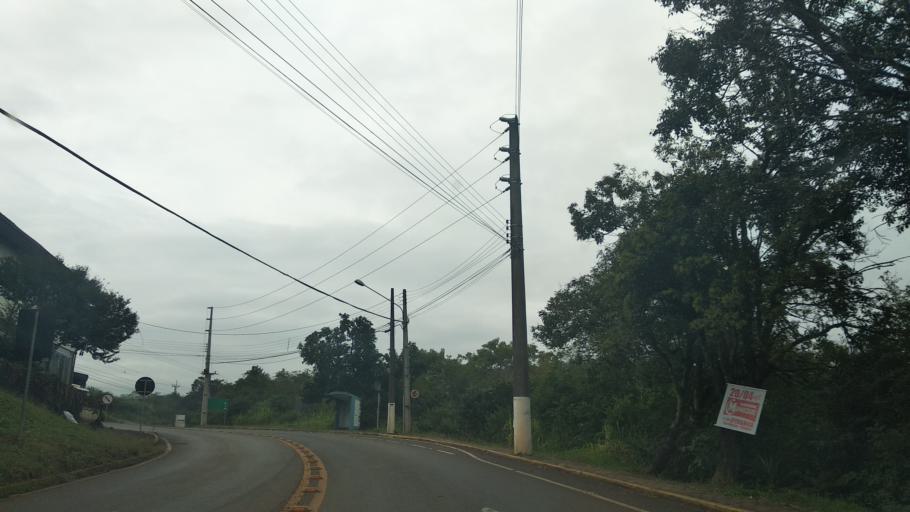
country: BR
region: Santa Catarina
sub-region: Videira
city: Videira
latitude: -27.0552
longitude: -51.2297
